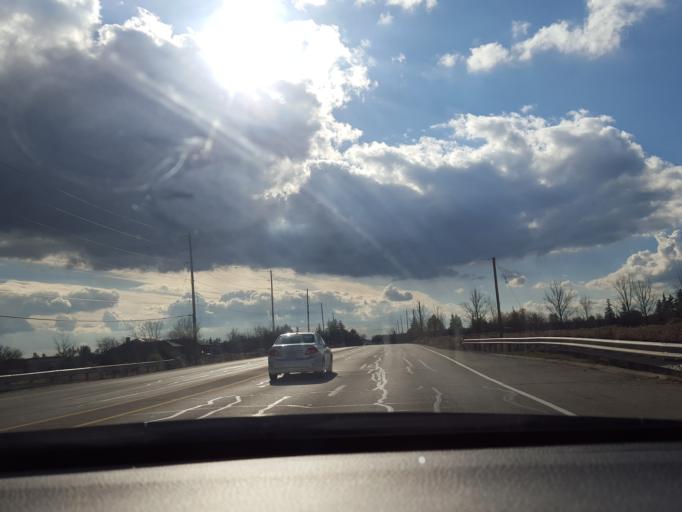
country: CA
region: Ontario
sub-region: Halton
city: Milton
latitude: 43.5505
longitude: -79.8135
